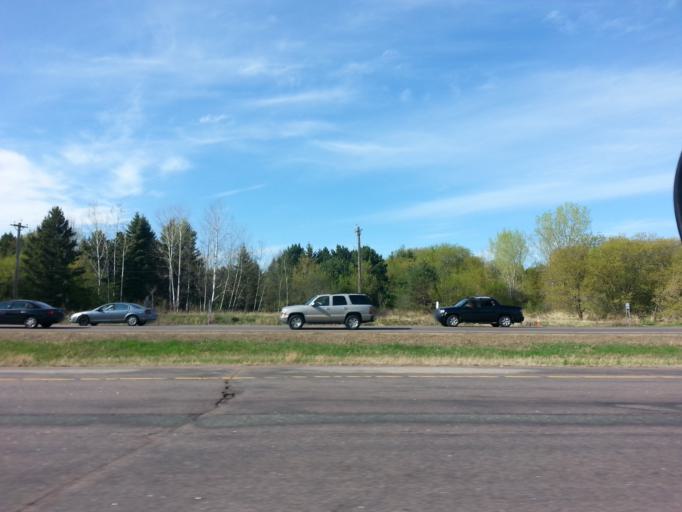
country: US
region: Minnesota
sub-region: Washington County
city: Lake Elmo
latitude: 45.0356
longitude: -92.8651
